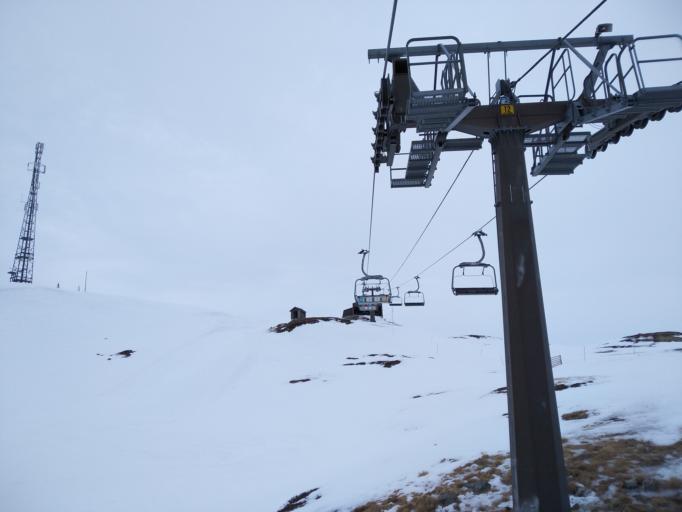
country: NO
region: Aust-Agder
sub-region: Bykle
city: Hovden
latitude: 59.5782
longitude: 7.3343
